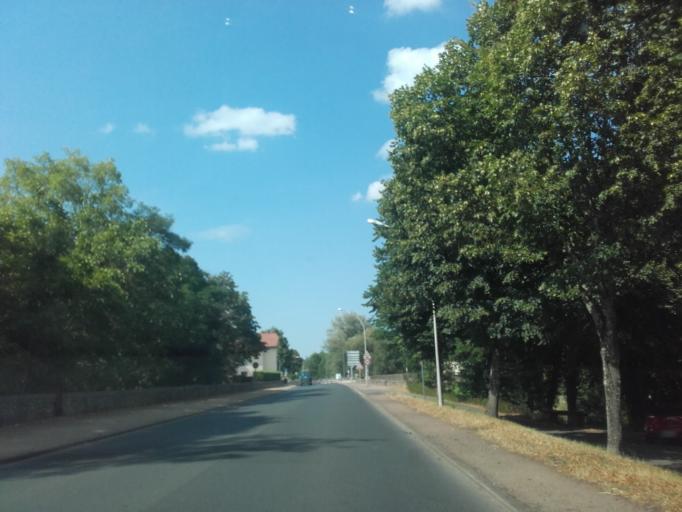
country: FR
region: Bourgogne
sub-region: Departement de Saone-et-Loire
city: Cluny
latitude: 46.4311
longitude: 4.6634
